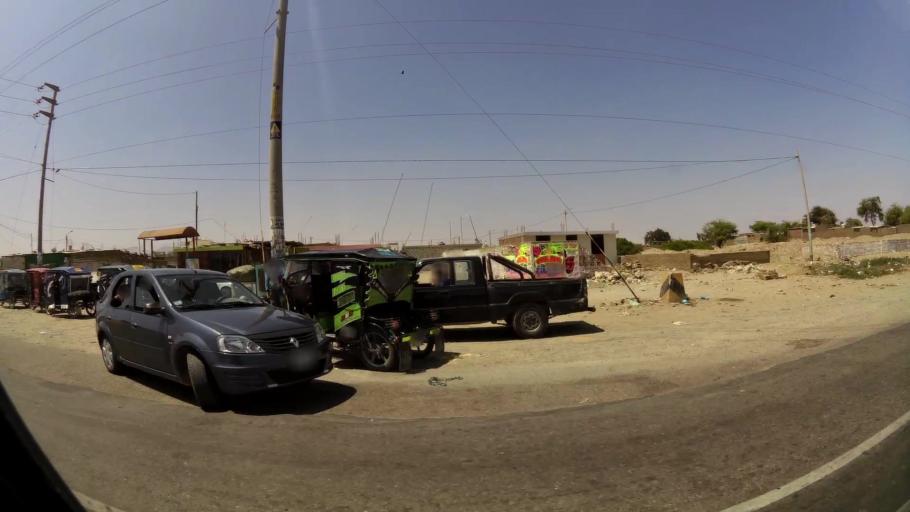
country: PE
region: La Libertad
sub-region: Provincia de Pacasmayo
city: San Pedro de Lloc
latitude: -7.4329
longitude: -79.5007
